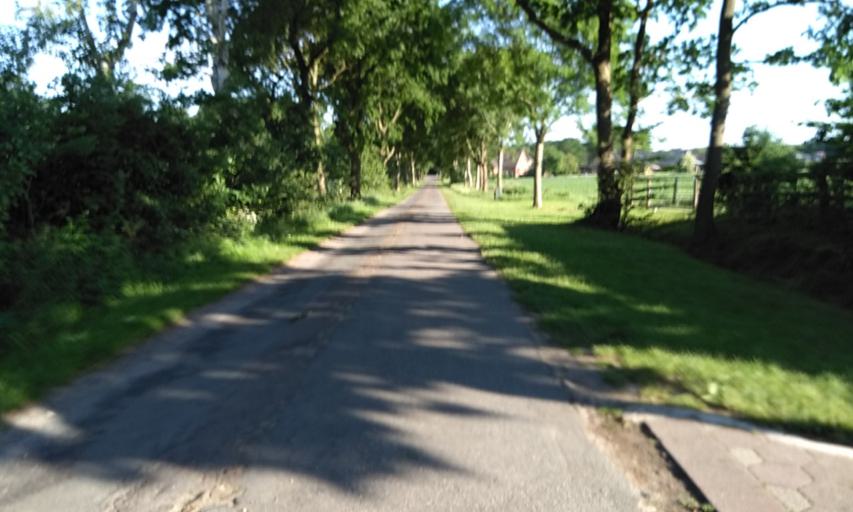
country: DE
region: Lower Saxony
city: Deinste
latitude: 53.5248
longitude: 9.4545
